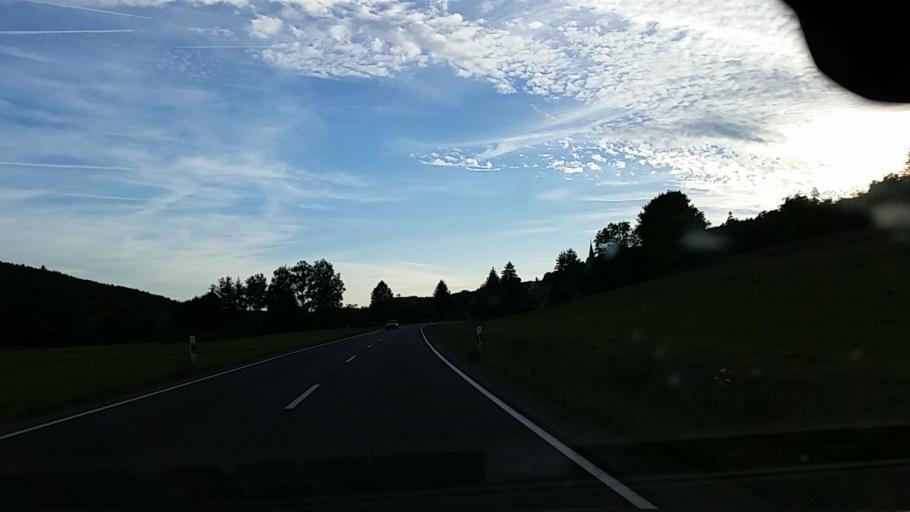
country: DE
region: Bavaria
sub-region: Regierungsbezirk Unterfranken
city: Thungen
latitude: 49.9626
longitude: 9.9026
